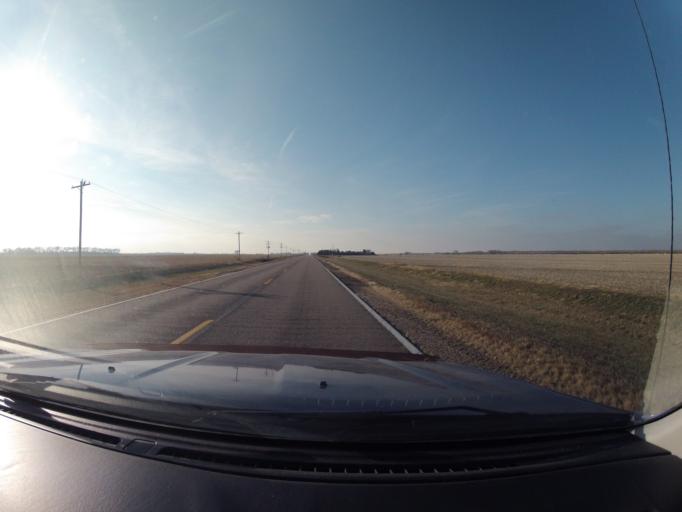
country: US
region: Nebraska
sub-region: Buffalo County
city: Kearney
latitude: 40.6410
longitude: -99.0484
